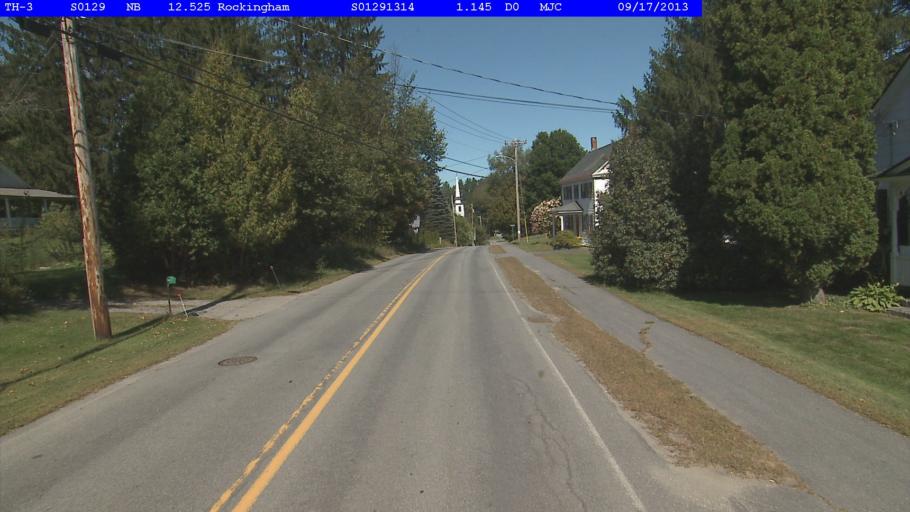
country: US
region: Vermont
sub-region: Windham County
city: Rockingham
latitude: 43.1360
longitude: -72.5106
